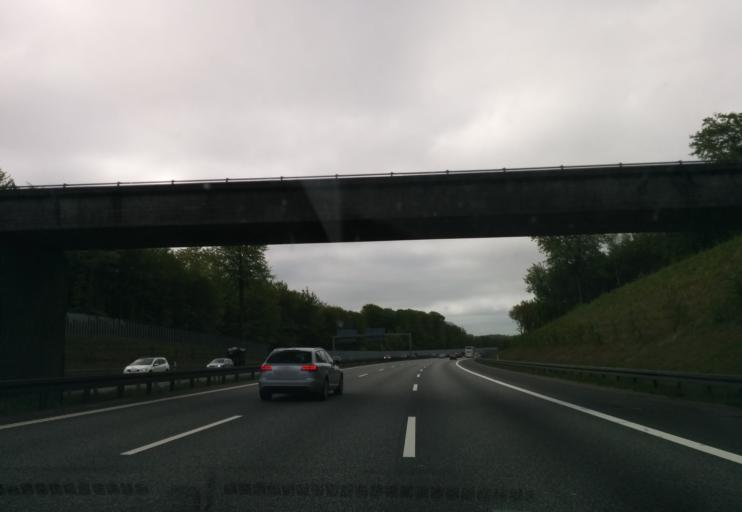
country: DK
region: South Denmark
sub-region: Vejle Kommune
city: Vejle
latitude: 55.7125
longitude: 9.5766
